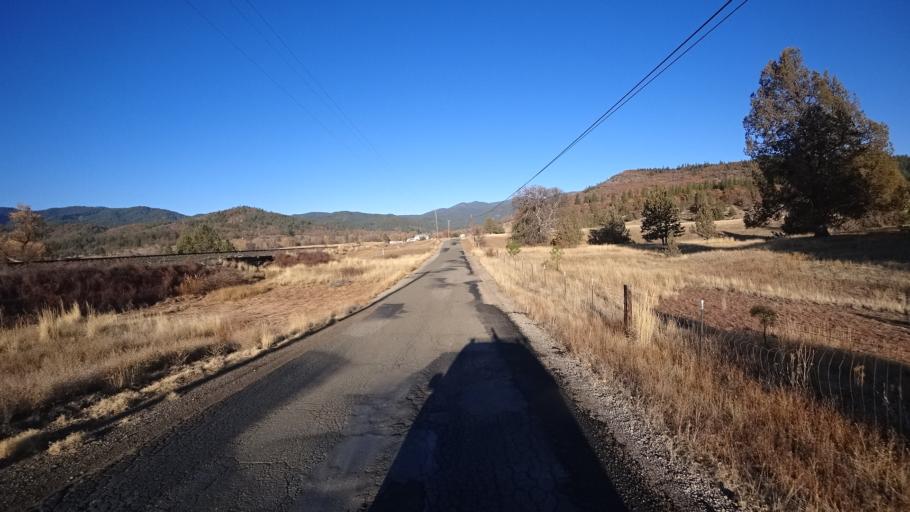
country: US
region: Oregon
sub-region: Jackson County
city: Ashland
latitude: 41.9989
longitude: -122.6324
